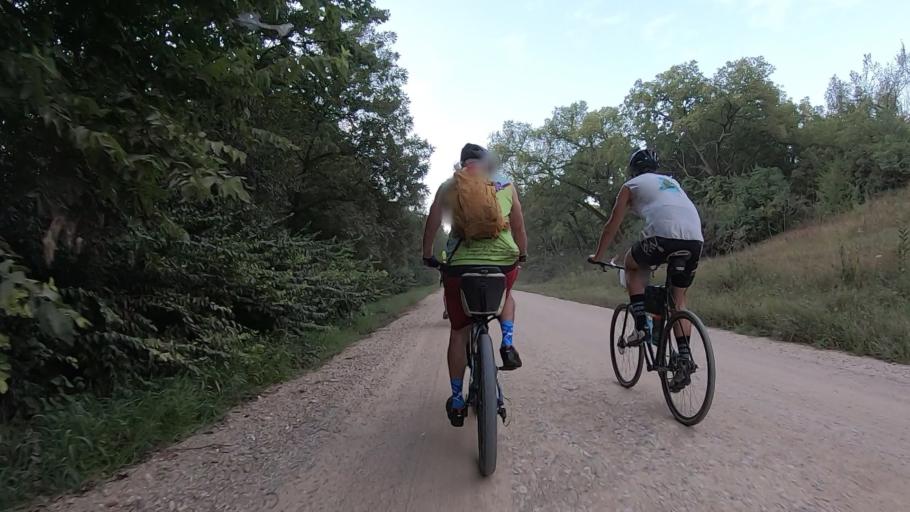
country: US
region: Kansas
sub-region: Marshall County
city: Marysville
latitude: 39.8327
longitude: -96.6650
